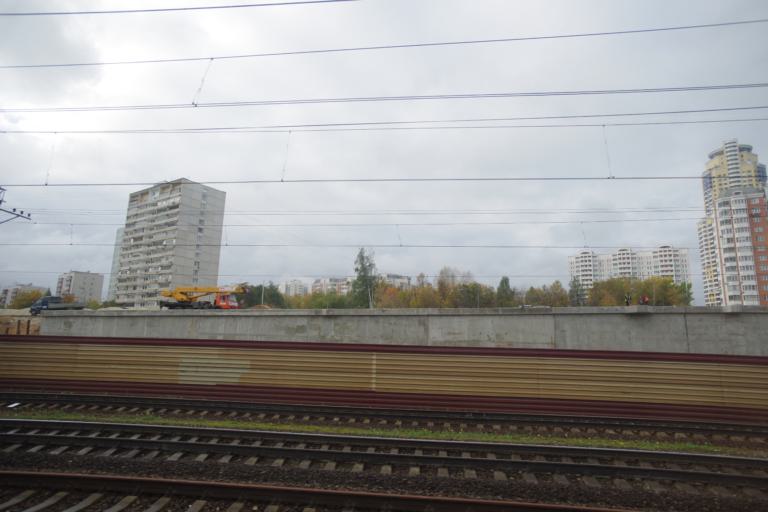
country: RU
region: Moskovskaya
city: Levoberezhnaya
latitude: 55.8786
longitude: 37.4888
